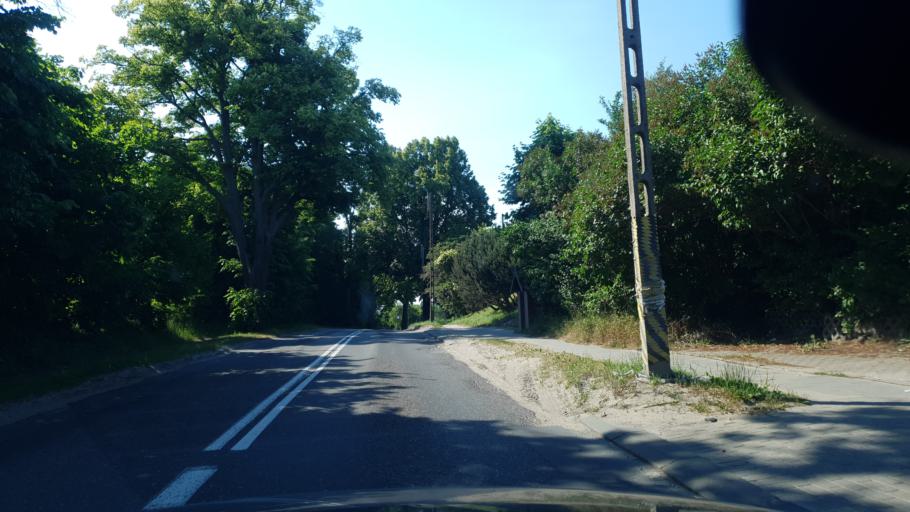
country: PL
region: Pomeranian Voivodeship
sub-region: Gdynia
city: Wielki Kack
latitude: 54.4356
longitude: 18.4648
